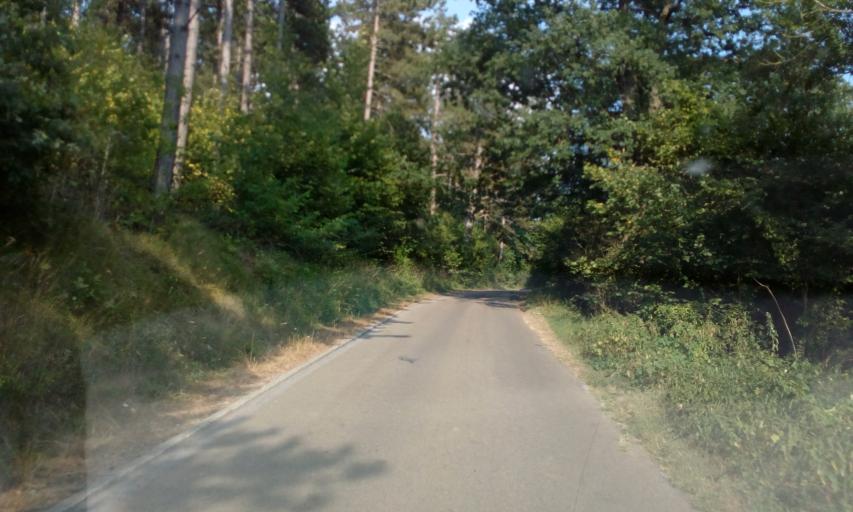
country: BE
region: Wallonia
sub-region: Province du Luxembourg
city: Tellin
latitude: 50.1093
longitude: 5.2217
